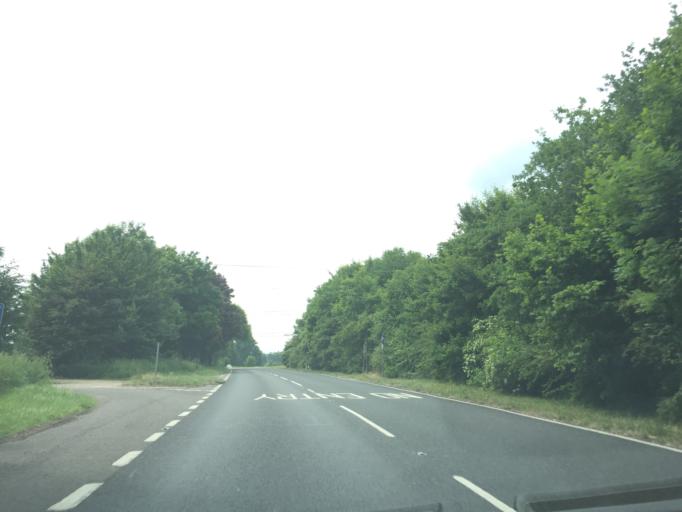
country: GB
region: England
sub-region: Hampshire
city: Long Sutton
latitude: 51.1830
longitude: -0.9033
